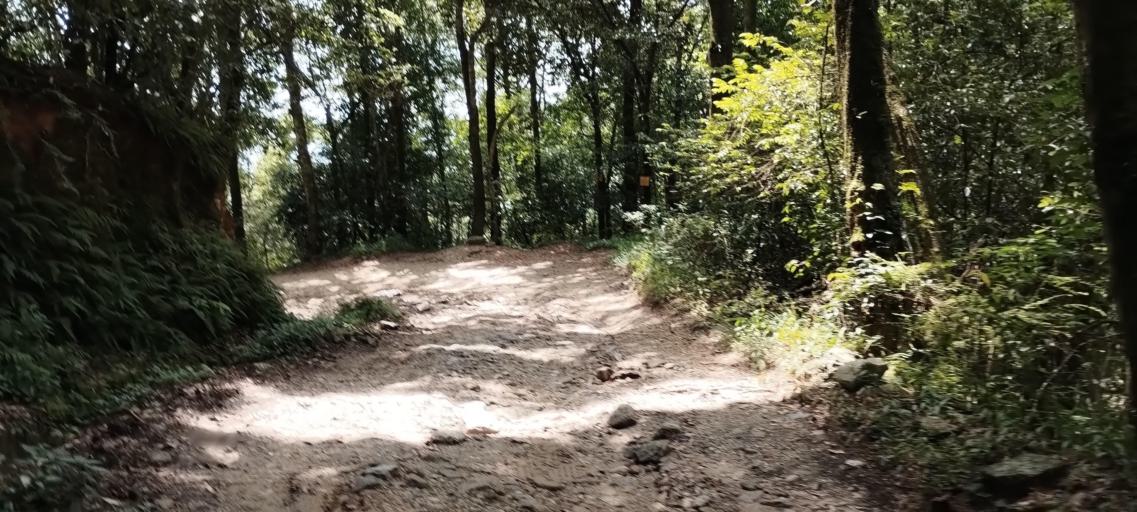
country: NP
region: Central Region
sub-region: Bagmati Zone
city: Kathmandu
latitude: 27.7911
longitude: 85.3732
